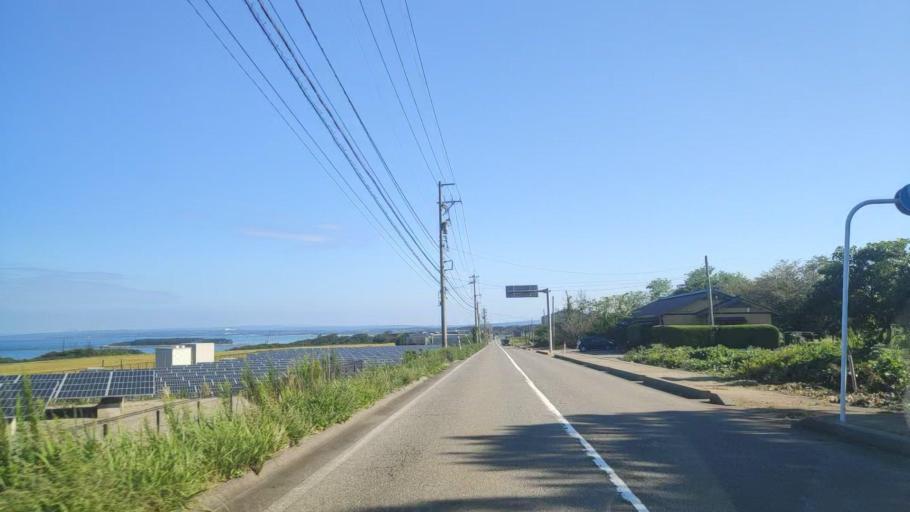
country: JP
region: Ishikawa
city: Hakui
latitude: 36.9342
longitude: 136.7572
